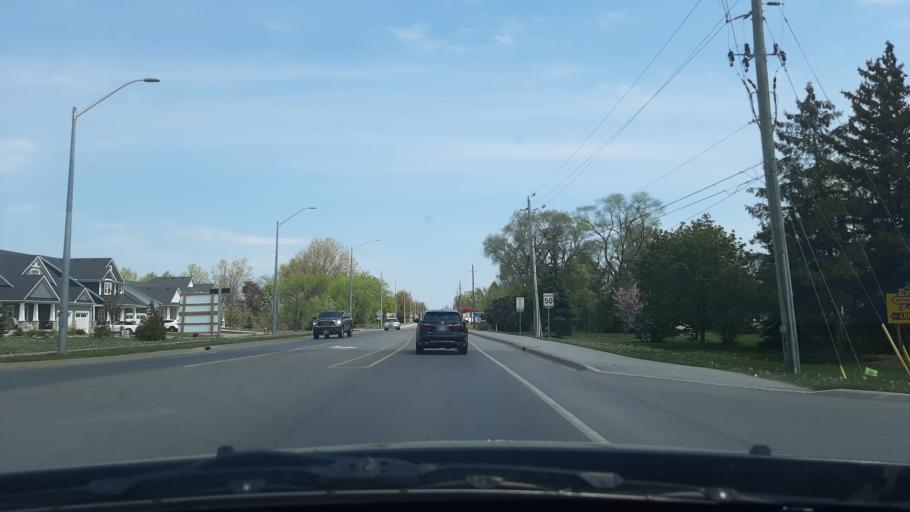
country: US
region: New York
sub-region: Niagara County
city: Youngstown
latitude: 43.2117
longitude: -79.1351
